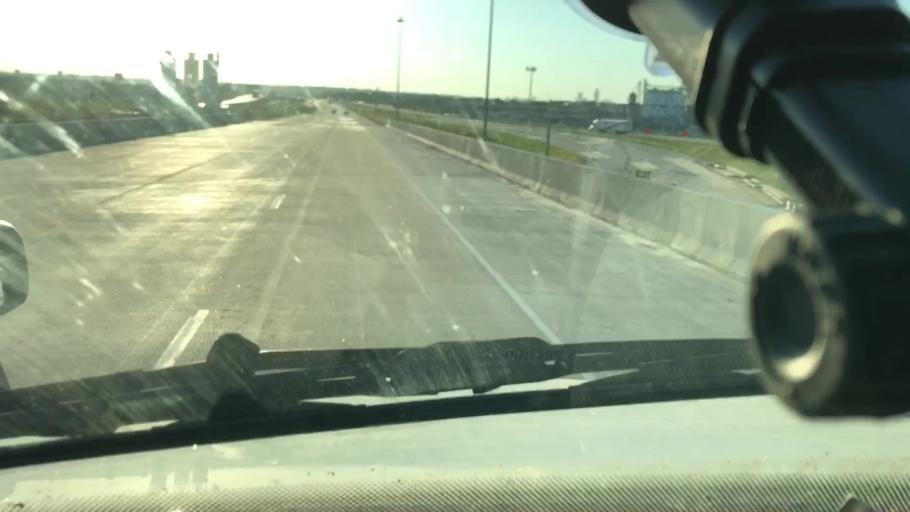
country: US
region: Iowa
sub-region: Pottawattamie County
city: Council Bluffs
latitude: 41.2324
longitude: -95.8428
